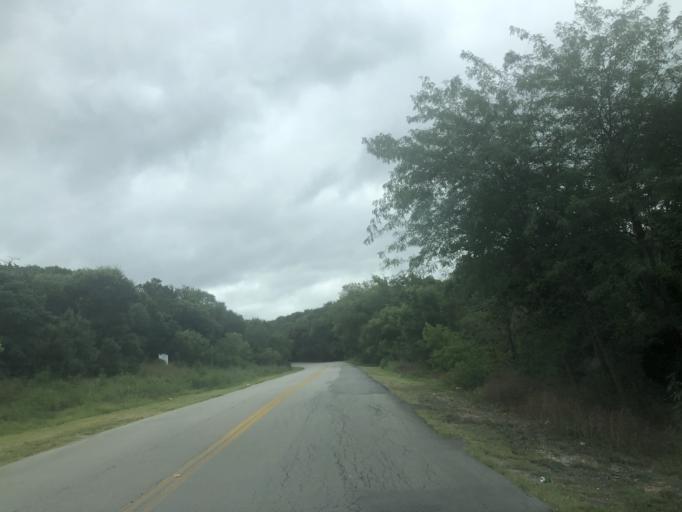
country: US
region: Texas
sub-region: Dallas County
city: Duncanville
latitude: 32.6656
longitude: -96.9580
